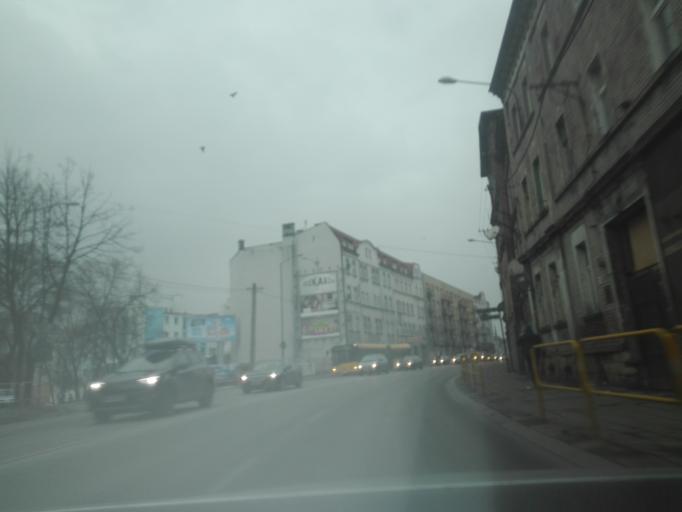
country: PL
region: Silesian Voivodeship
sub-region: Chorzow
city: Chorzow
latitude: 50.2928
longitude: 18.9579
